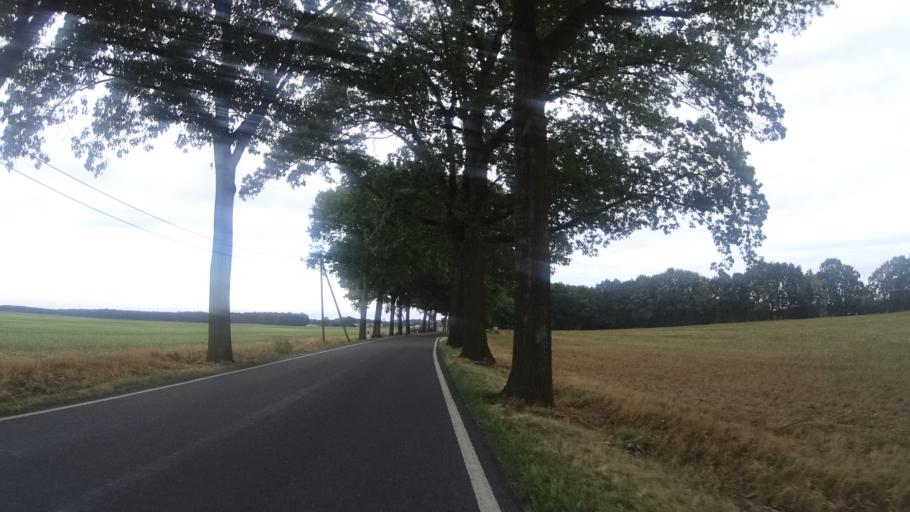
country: DE
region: Saxony
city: Rothenburg
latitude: 51.3027
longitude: 15.0077
